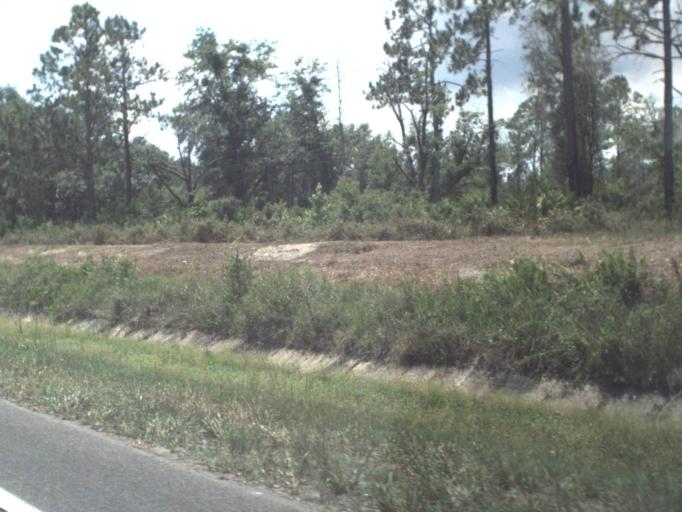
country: US
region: Florida
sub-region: Putnam County
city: Palatka
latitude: 29.4947
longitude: -81.7449
